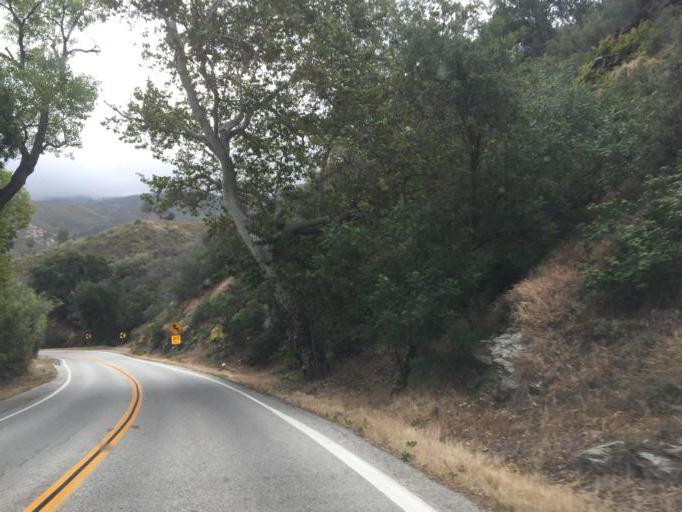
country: US
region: California
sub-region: Los Angeles County
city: Green Valley
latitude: 34.5535
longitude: -118.4129
